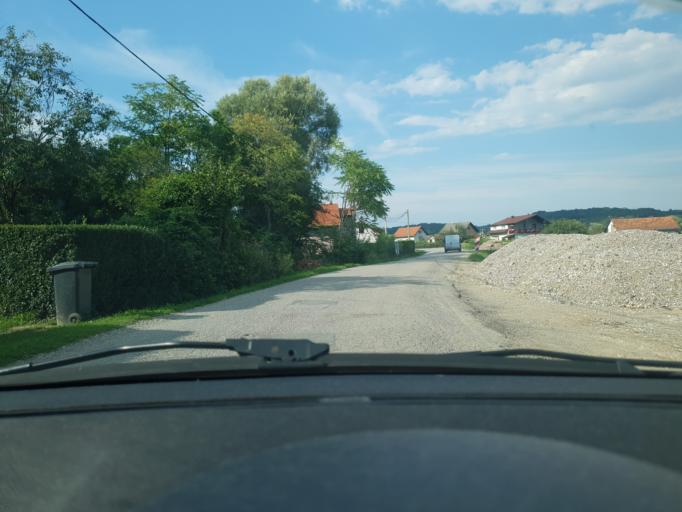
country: HR
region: Zagrebacka
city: Jakovlje
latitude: 46.0317
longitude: 15.8255
